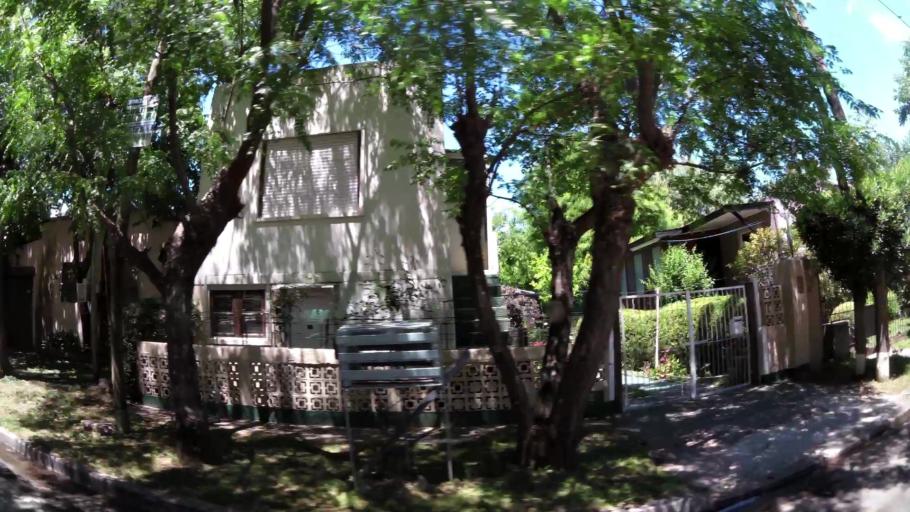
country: AR
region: Buenos Aires
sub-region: Partido de Tigre
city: Tigre
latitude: -34.4419
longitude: -58.5451
